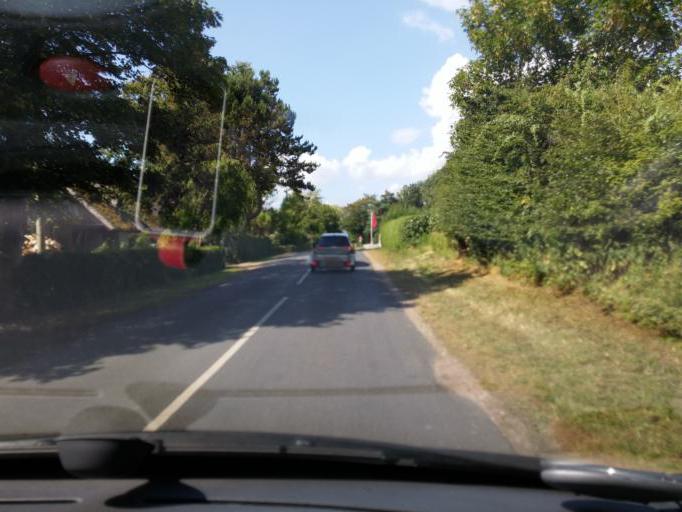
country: DK
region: South Denmark
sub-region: AEro Kommune
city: Marstal
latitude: 54.8189
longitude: 10.6404
